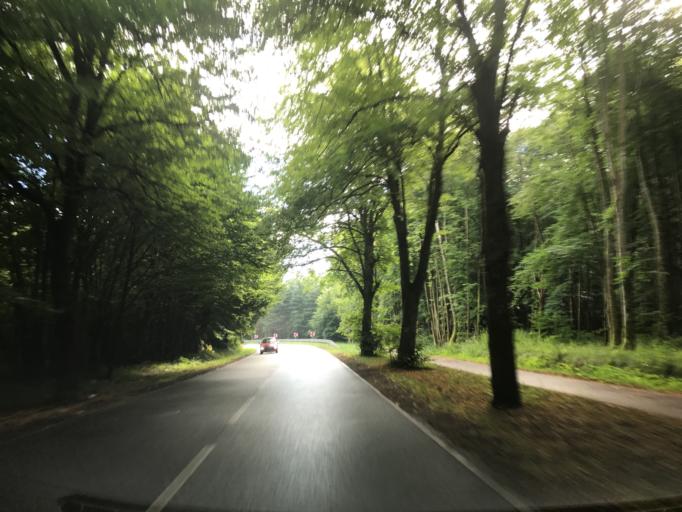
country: PL
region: West Pomeranian Voivodeship
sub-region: Powiat koszalinski
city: Sianow
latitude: 54.2133
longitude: 16.2716
